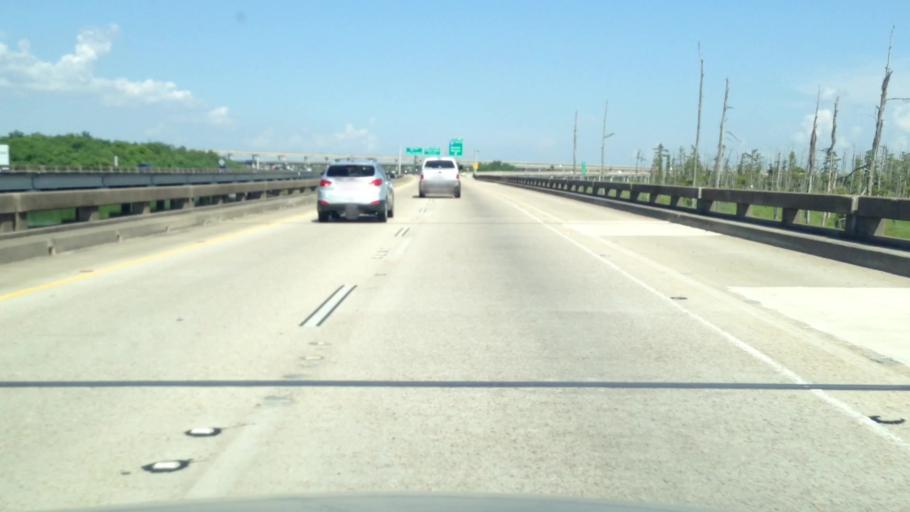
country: US
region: Louisiana
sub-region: Saint Charles Parish
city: Ama
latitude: 30.0085
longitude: -90.3010
